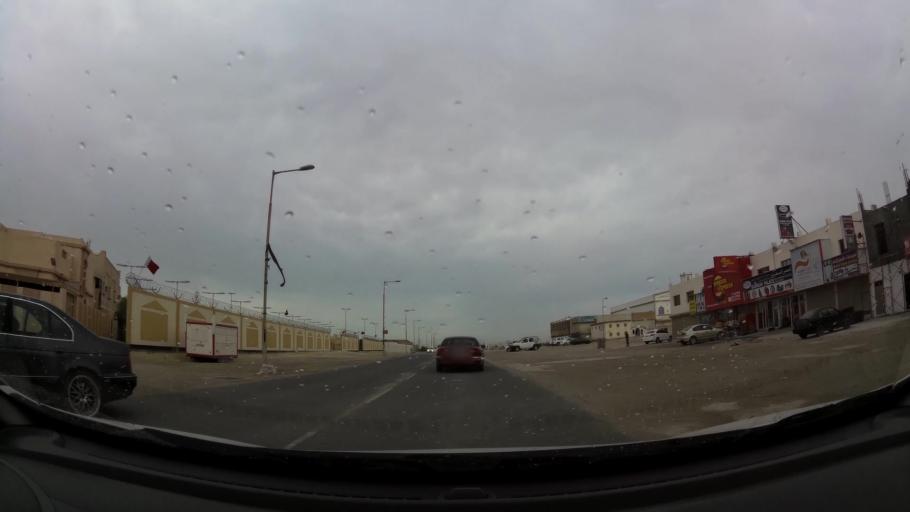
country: BH
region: Central Governorate
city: Madinat Hamad
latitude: 26.1296
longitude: 50.4785
